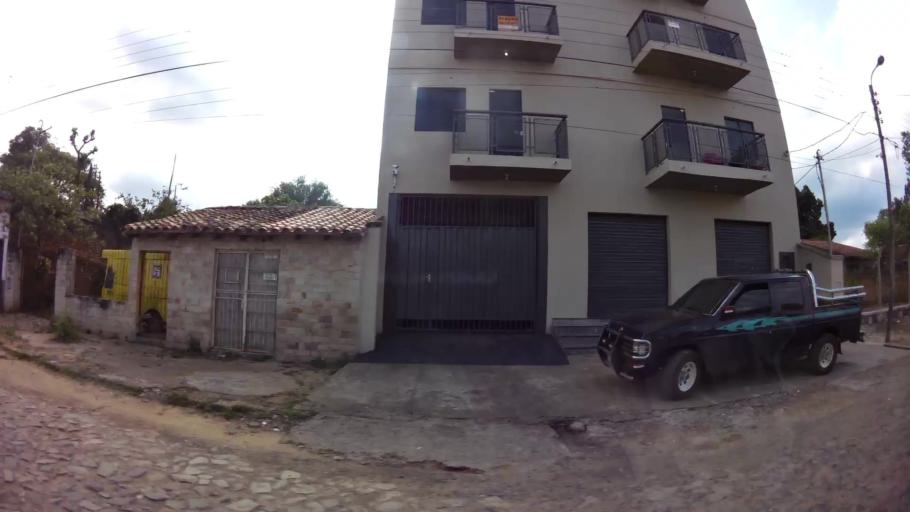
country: PY
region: Central
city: Fernando de la Mora
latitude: -25.3474
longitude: -57.5437
